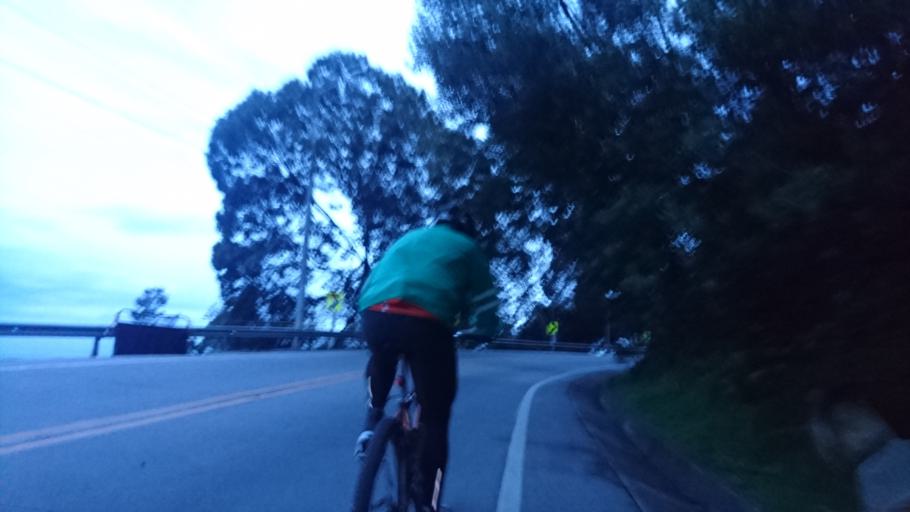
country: CO
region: Bogota D.C.
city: Barrio San Luis
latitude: 4.6759
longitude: -74.0357
